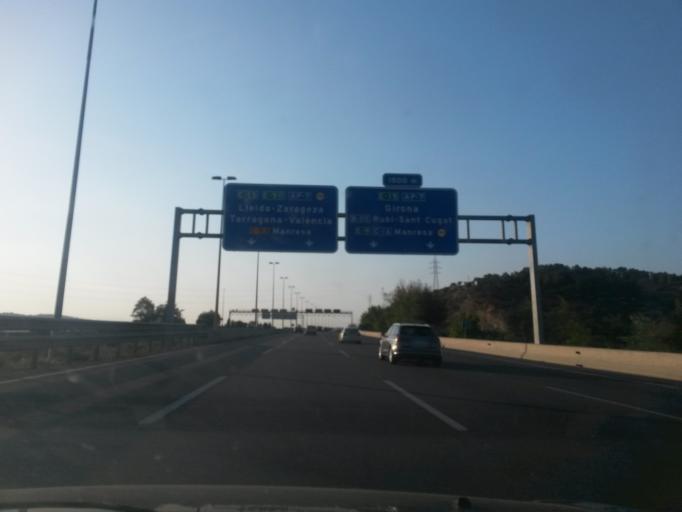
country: ES
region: Catalonia
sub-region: Provincia de Barcelona
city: Molins de Rei
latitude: 41.4199
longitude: 2.0085
